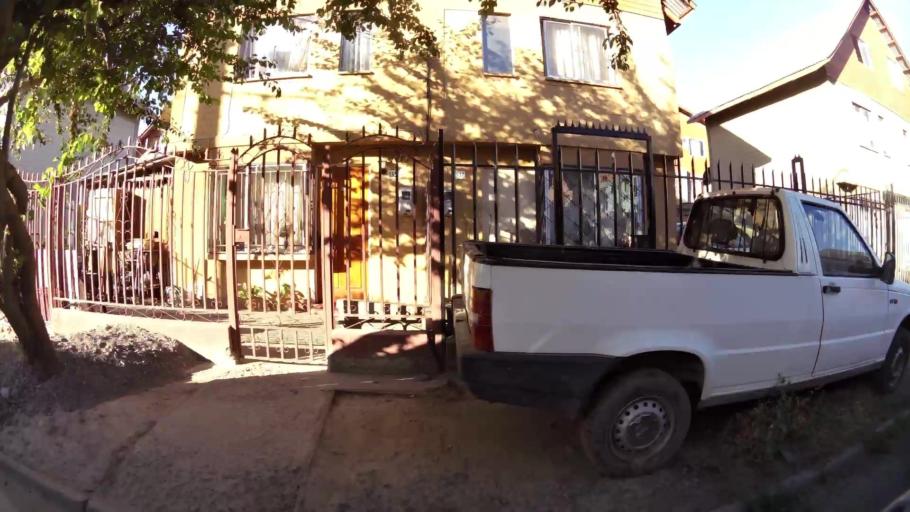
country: CL
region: O'Higgins
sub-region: Provincia de Cachapoal
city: Rancagua
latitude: -34.1847
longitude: -70.7659
